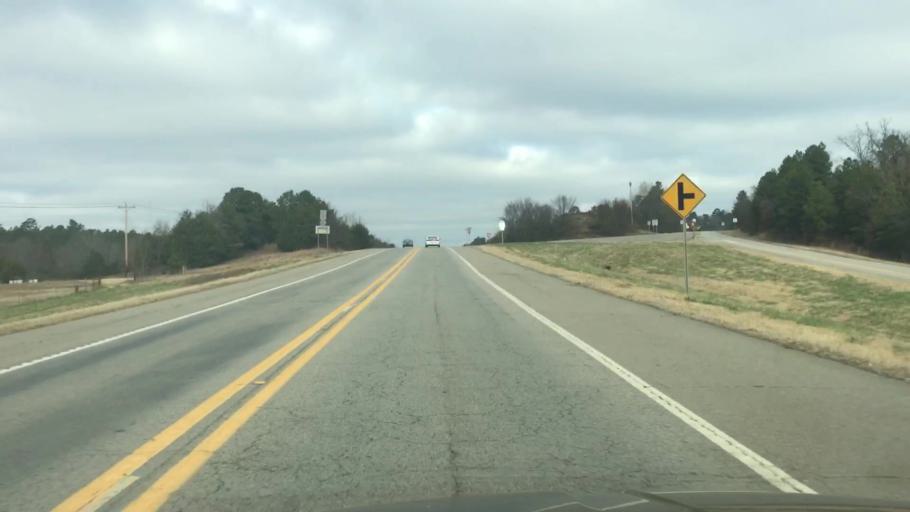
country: US
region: Arkansas
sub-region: Scott County
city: Waldron
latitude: 34.8552
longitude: -94.0664
